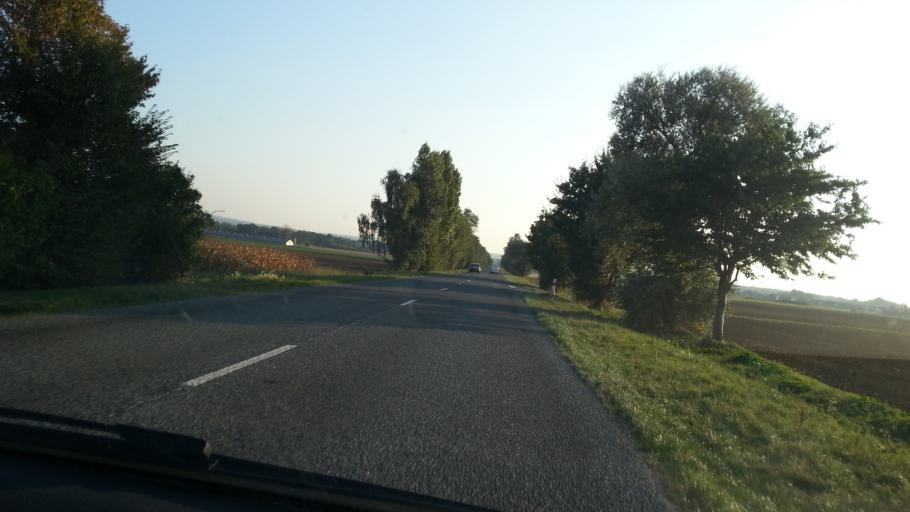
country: FR
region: Picardie
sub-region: Departement de l'Oise
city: Saint-Martin-Longueau
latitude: 49.3527
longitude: 2.6098
